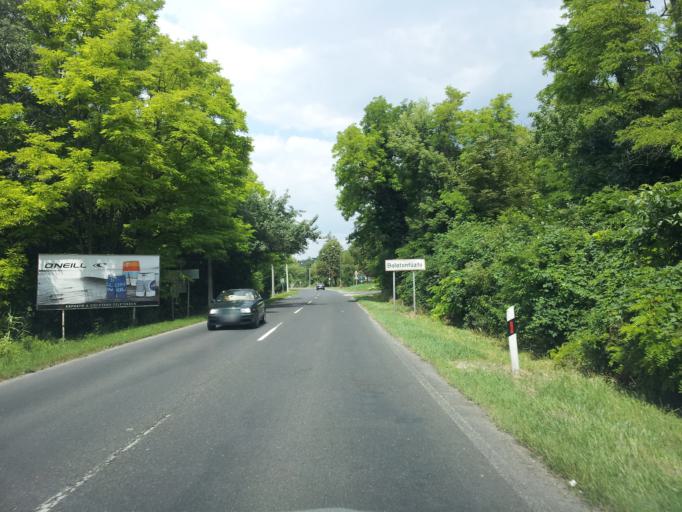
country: HU
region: Veszprem
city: Balatonalmadi
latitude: 47.0463
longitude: 18.0587
